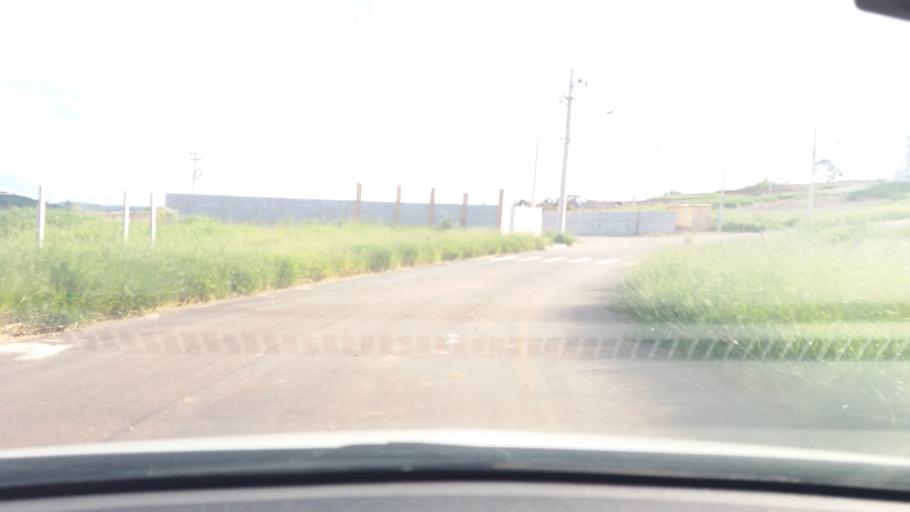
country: BR
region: Sao Paulo
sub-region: Bom Jesus Dos Perdoes
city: Bom Jesus dos Perdoes
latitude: -23.1535
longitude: -46.4728
